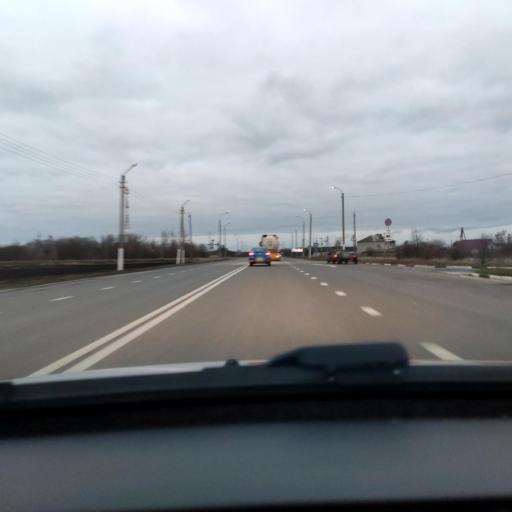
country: RU
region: Lipetsk
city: Borinskoye
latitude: 52.4614
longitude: 39.3267
